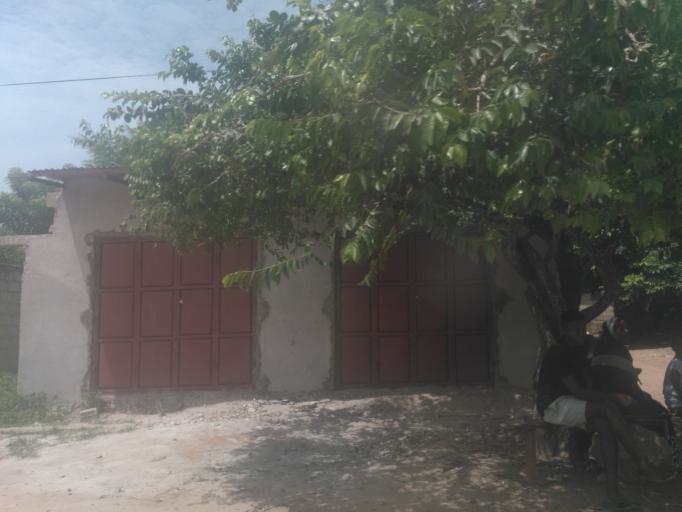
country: TZ
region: Zanzibar Urban/West
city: Zanzibar
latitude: -6.2251
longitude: 39.2141
